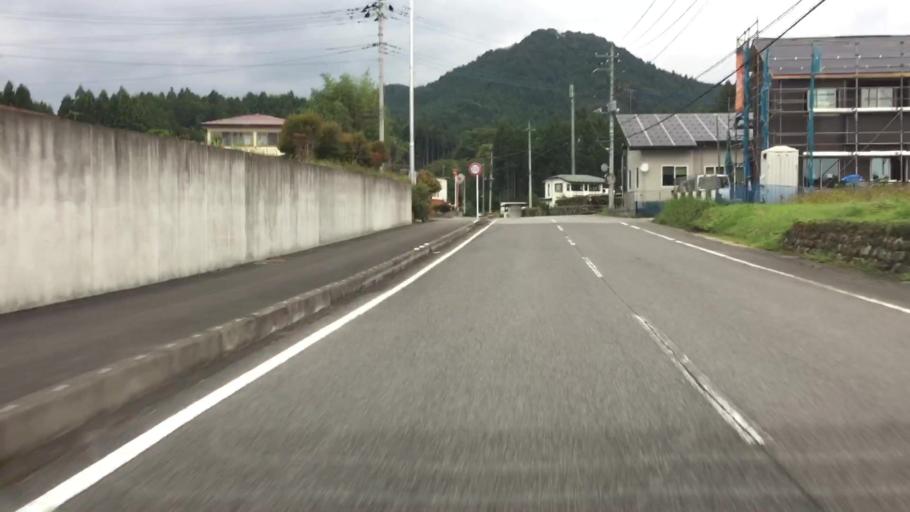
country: JP
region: Tochigi
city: Imaichi
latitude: 36.7449
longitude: 139.6849
